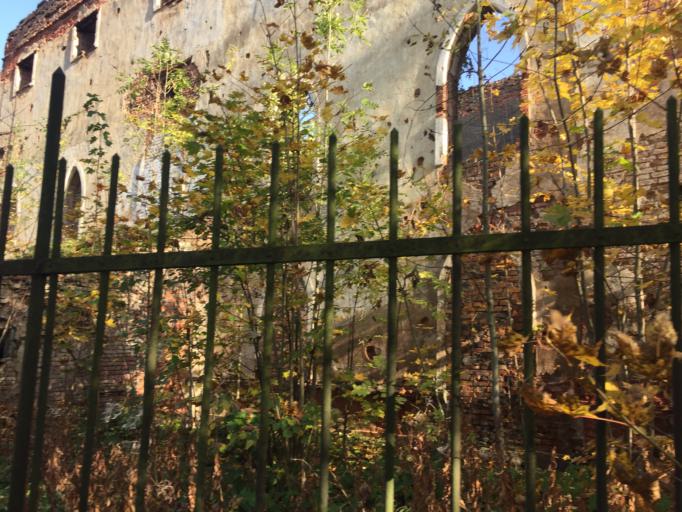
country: RU
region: St.-Petersburg
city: Pushkin
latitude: 59.7179
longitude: 30.3856
